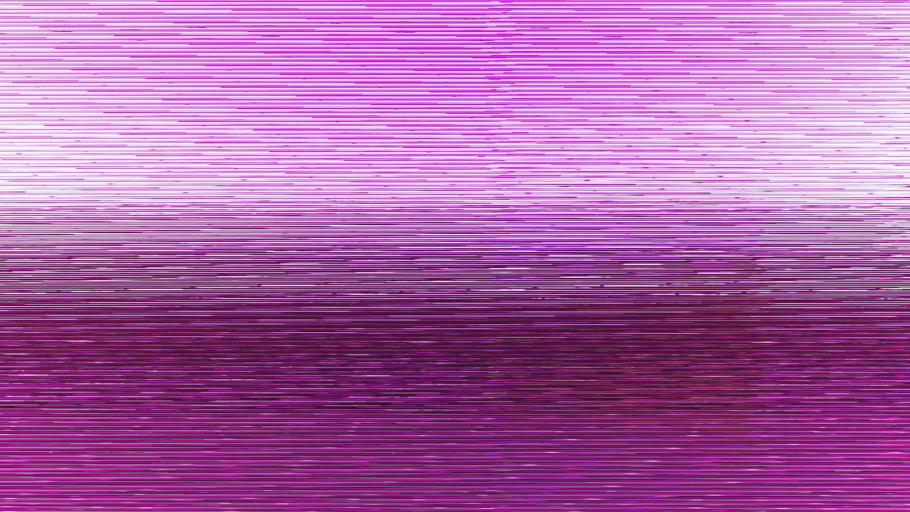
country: US
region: Michigan
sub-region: Washtenaw County
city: Ypsilanti
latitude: 42.2253
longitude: -83.6323
